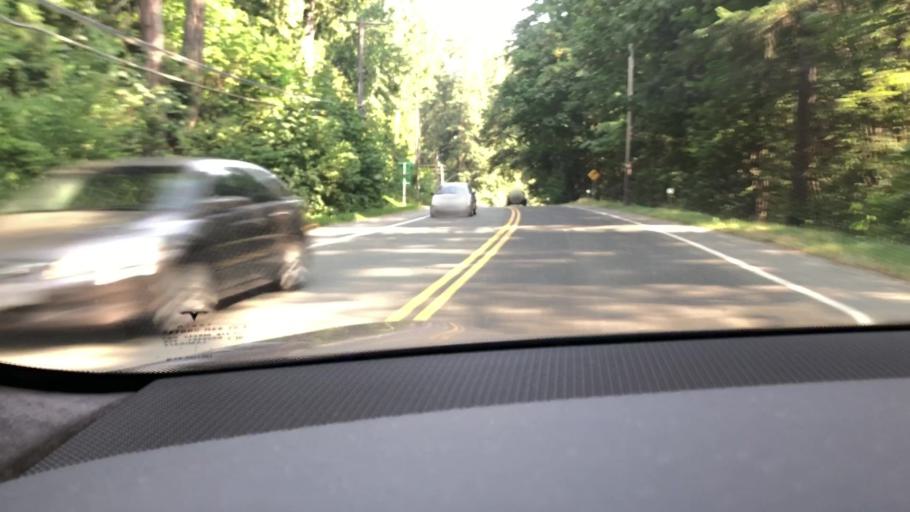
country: CA
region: British Columbia
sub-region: Fraser Valley Regional District
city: Chilliwack
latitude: 49.0795
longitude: -121.9797
